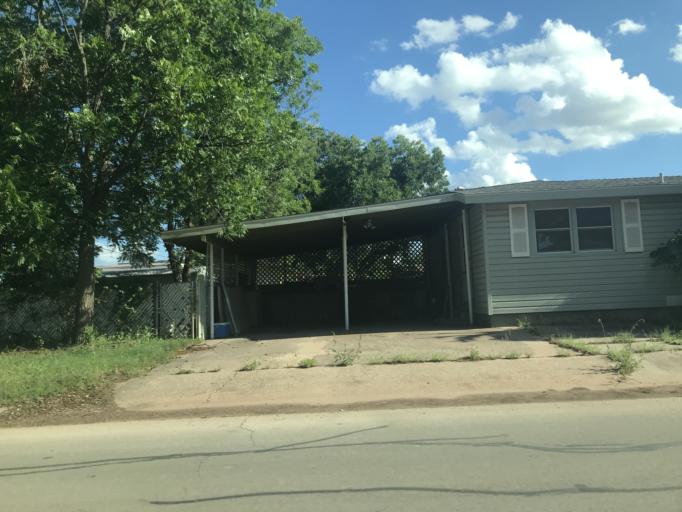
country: US
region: Texas
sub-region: Taylor County
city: Abilene
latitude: 32.4360
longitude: -99.7808
